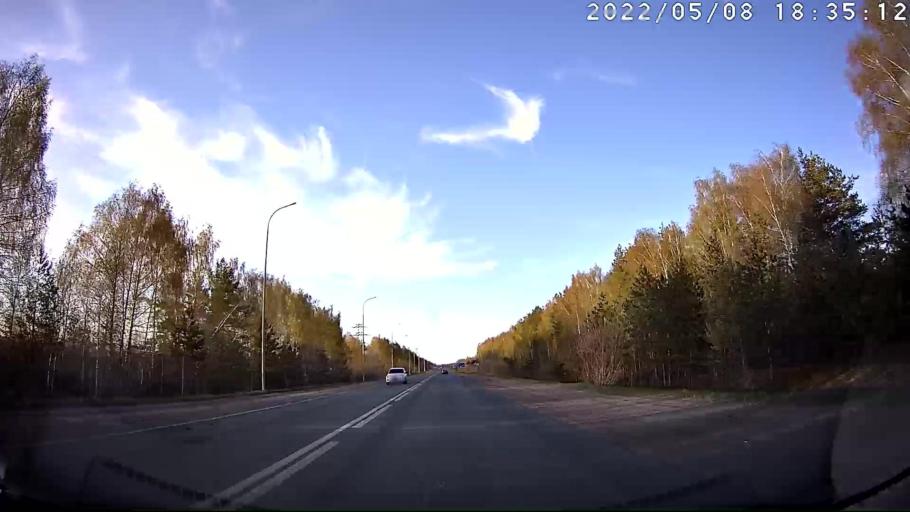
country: RU
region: Mariy-El
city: Volzhsk
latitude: 55.9067
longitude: 48.3602
